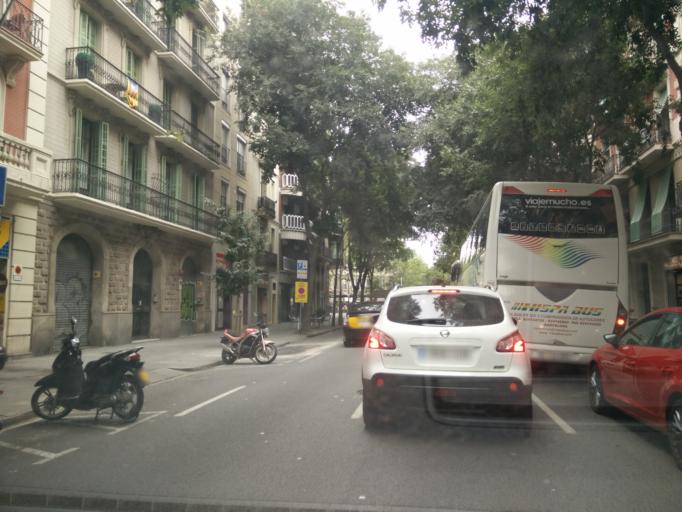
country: ES
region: Catalonia
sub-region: Provincia de Barcelona
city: Sants-Montjuic
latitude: 41.3773
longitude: 2.1538
